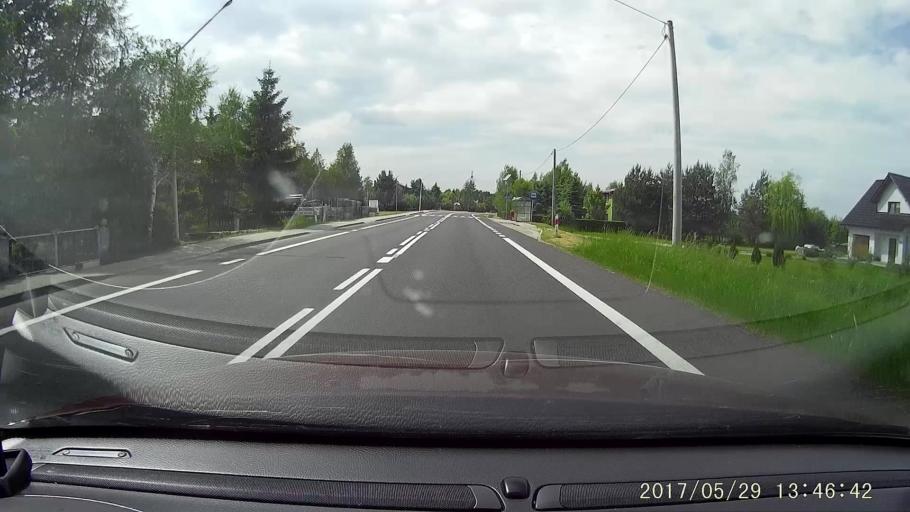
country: PL
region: Lower Silesian Voivodeship
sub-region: Powiat lubanski
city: Siekierczyn
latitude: 51.1515
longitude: 15.1638
